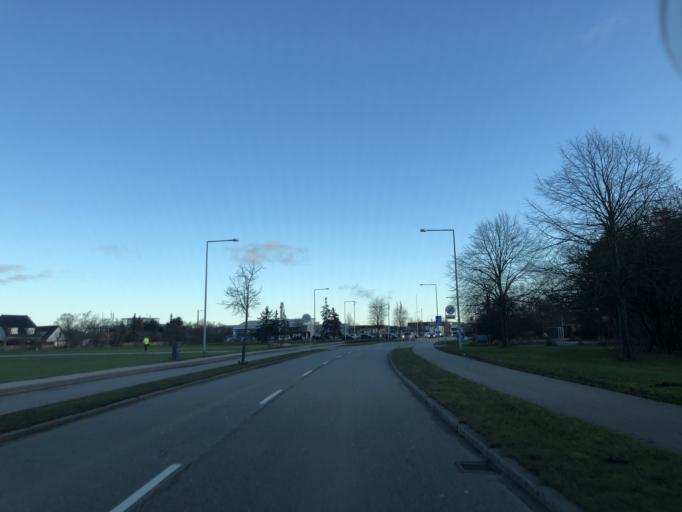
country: DK
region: Capital Region
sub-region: Tarnby Kommune
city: Tarnby
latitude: 55.6118
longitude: 12.6103
